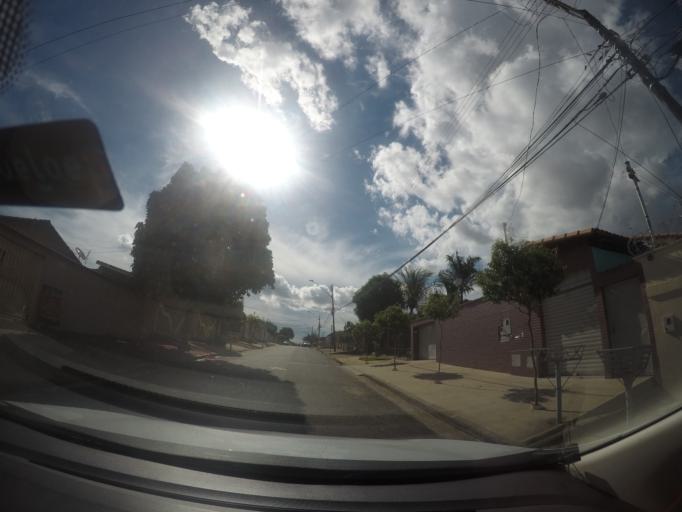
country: BR
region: Goias
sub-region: Goiania
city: Goiania
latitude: -16.6792
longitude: -49.3052
